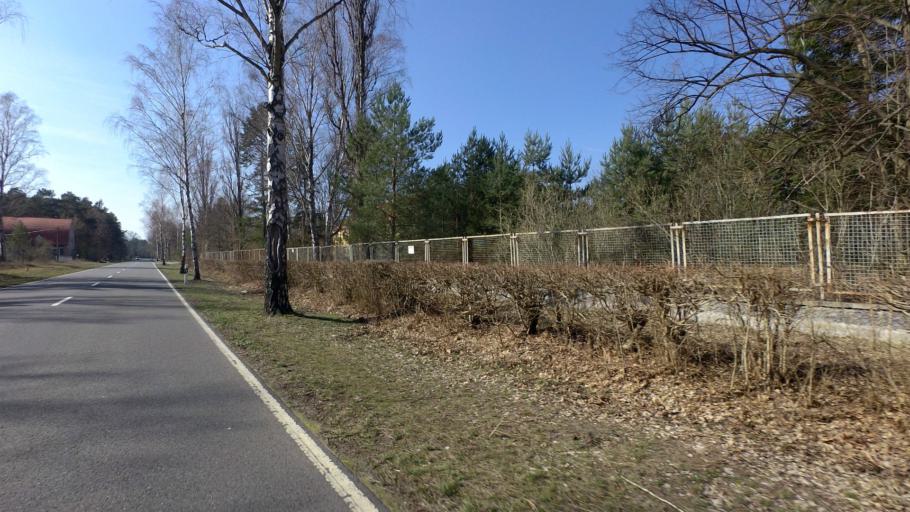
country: DE
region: Brandenburg
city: Sperenberg
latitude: 52.0958
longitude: 13.3643
